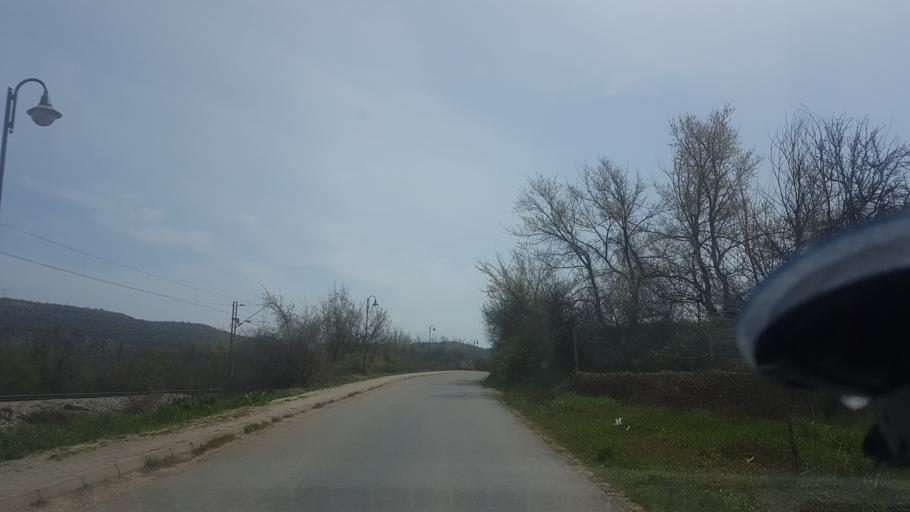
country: MK
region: Zelenikovo
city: Zelenikovo
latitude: 41.8824
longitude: 21.5941
